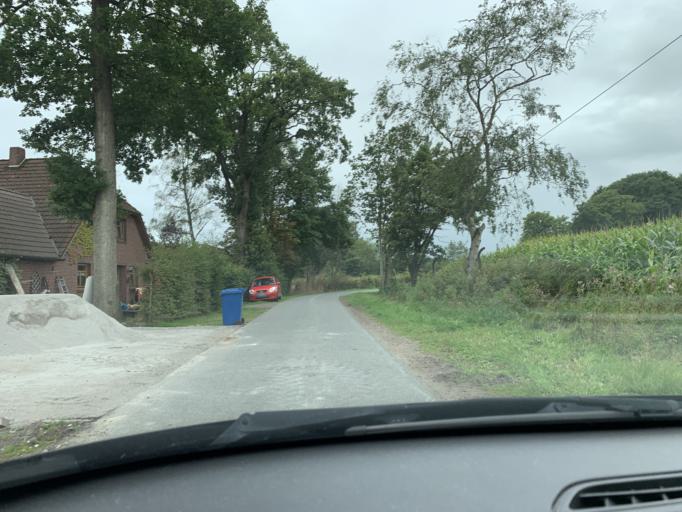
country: DE
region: Lower Saxony
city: Westerstede
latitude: 53.2646
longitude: 7.8914
